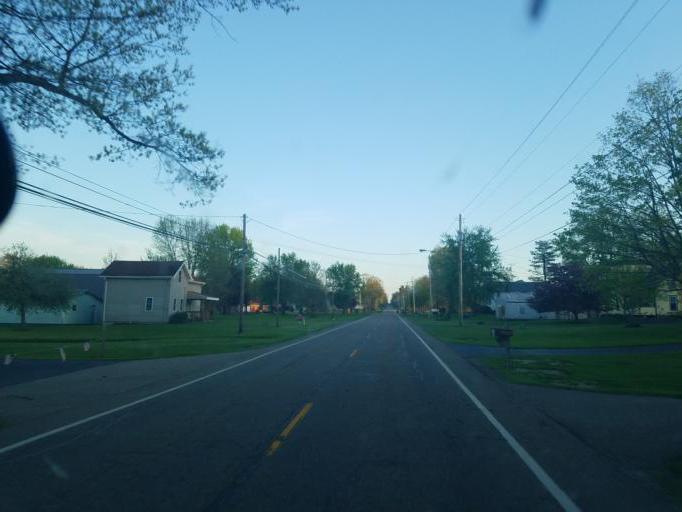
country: US
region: Ohio
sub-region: Trumbull County
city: Brookfield Center
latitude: 41.3562
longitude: -80.5692
